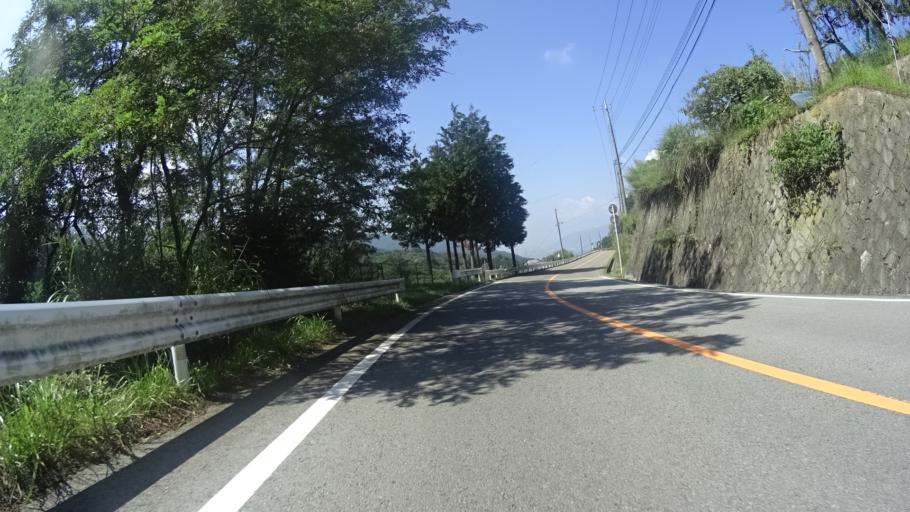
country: JP
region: Yamanashi
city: Enzan
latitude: 35.7352
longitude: 138.7973
